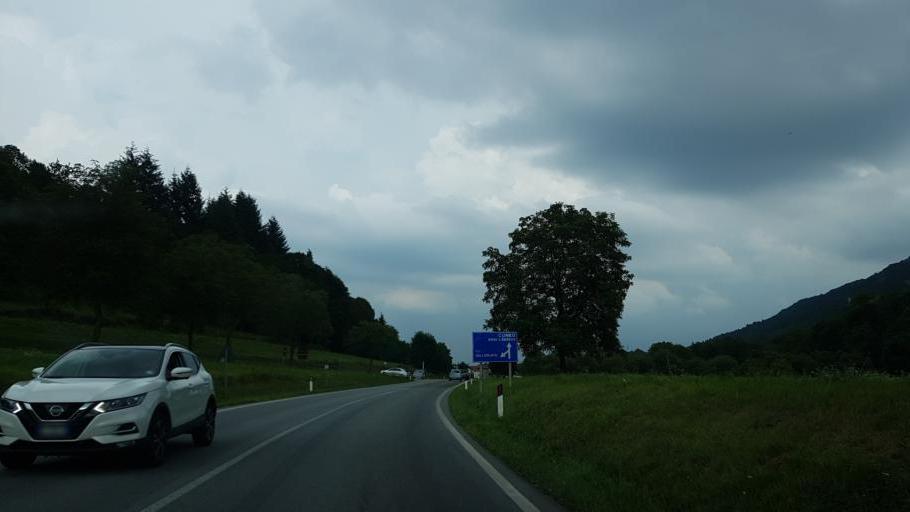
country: IT
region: Piedmont
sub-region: Provincia di Cuneo
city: Gaiola
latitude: 44.3321
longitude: 7.3976
